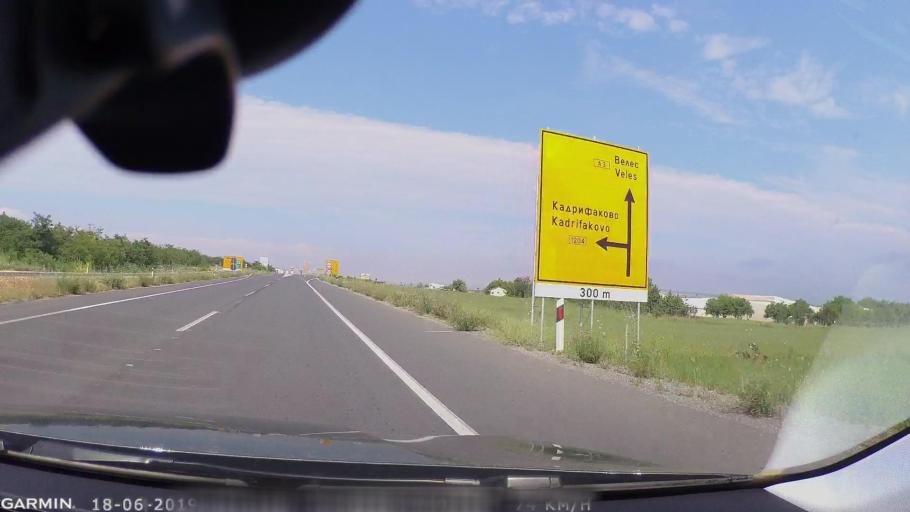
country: MK
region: Sveti Nikole
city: Sveti Nikole
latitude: 41.8262
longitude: 22.0072
